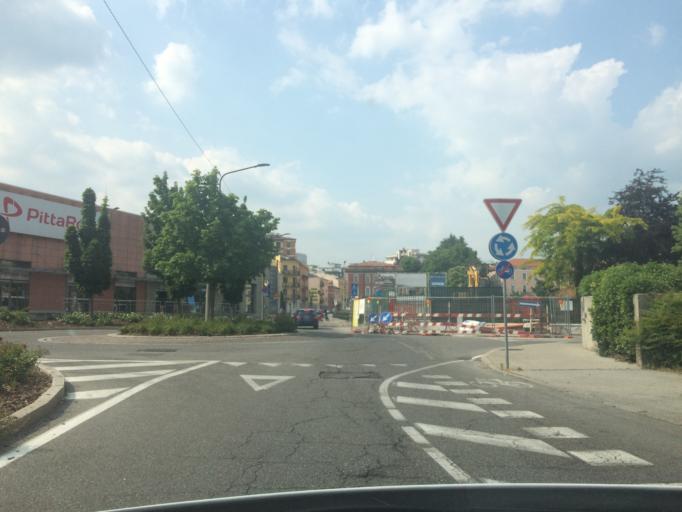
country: IT
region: Lombardy
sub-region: Provincia di Brescia
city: Brescia
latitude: 45.5324
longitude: 10.2360
